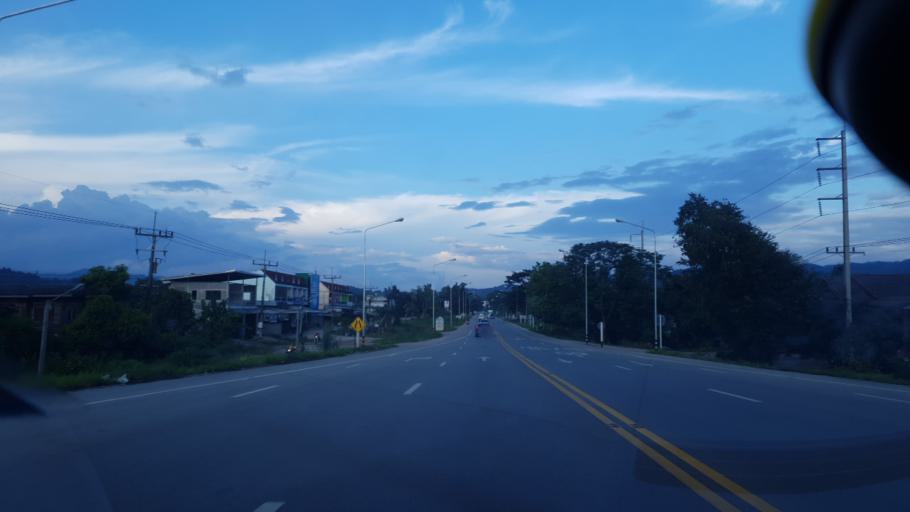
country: TH
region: Chiang Rai
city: Mae Suai
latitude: 19.6584
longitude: 99.5441
